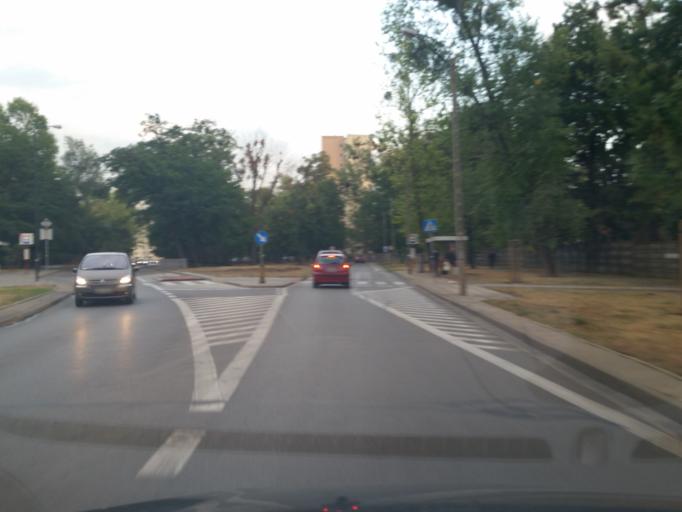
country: PL
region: Masovian Voivodeship
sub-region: Warszawa
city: Bemowo
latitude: 52.2554
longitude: 20.9051
